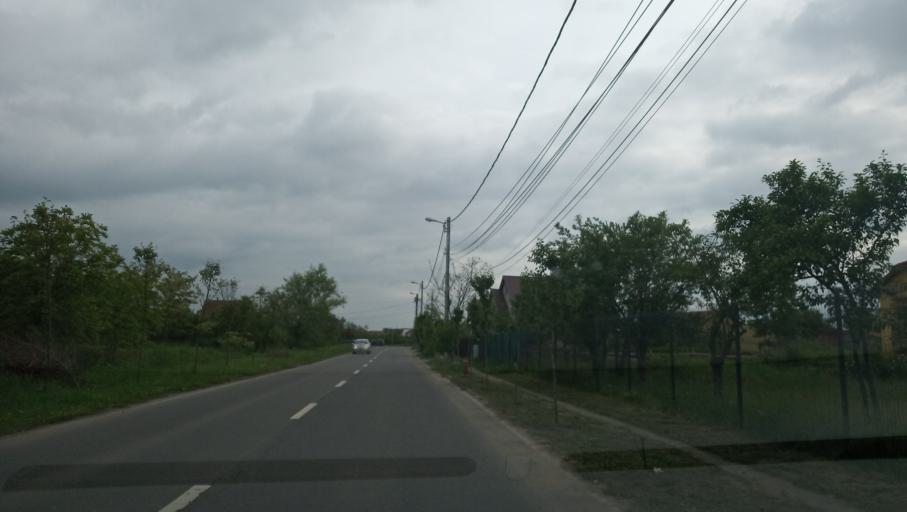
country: RO
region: Timis
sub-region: Comuna Ghiroda
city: Ghiroda
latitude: 45.7551
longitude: 21.2723
